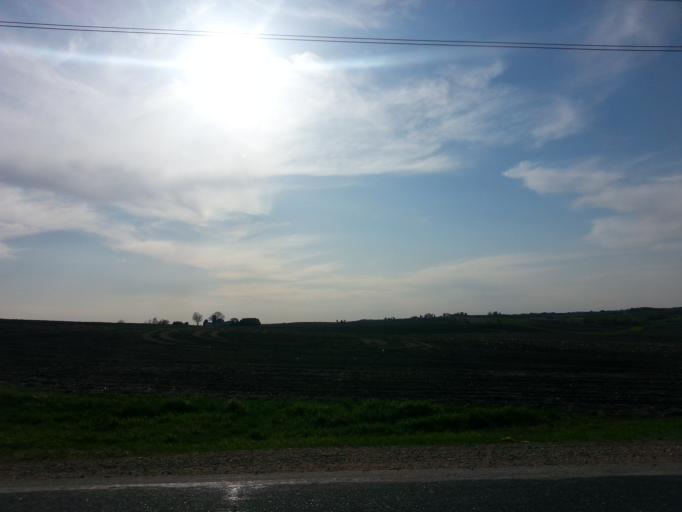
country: US
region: Wisconsin
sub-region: Pierce County
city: Ellsworth
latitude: 44.7119
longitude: -92.6091
